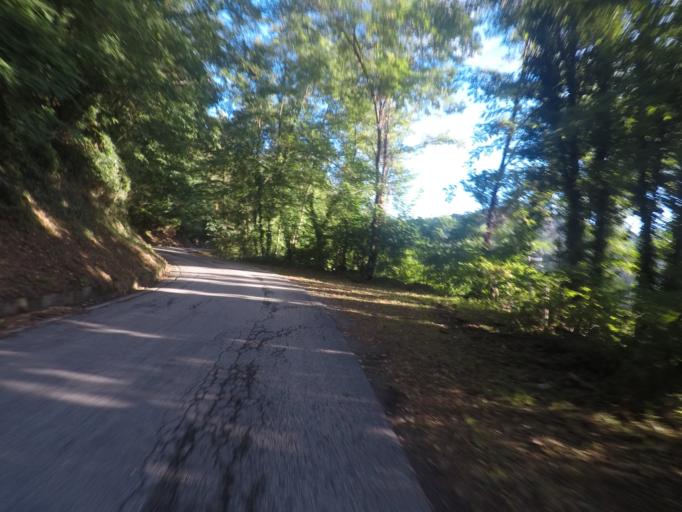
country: IT
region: Tuscany
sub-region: Provincia di Lucca
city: Massarosa
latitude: 43.9113
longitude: 10.3690
